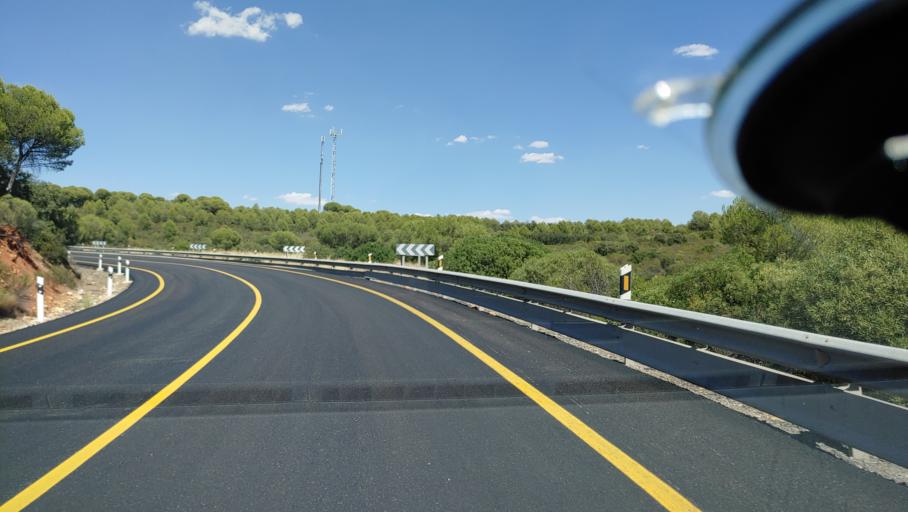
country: ES
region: Castille-La Mancha
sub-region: Provincia de Ciudad Real
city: Saceruela
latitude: 39.0154
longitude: -4.4572
